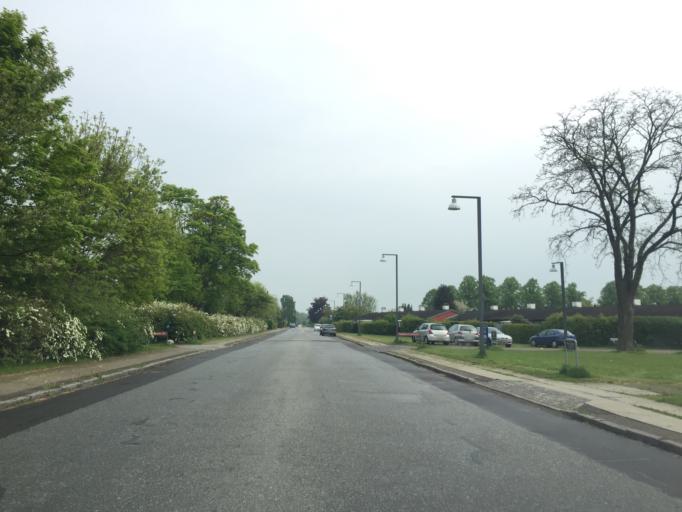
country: DK
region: Capital Region
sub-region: Rodovre Kommune
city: Rodovre
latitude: 55.6819
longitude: 12.4362
